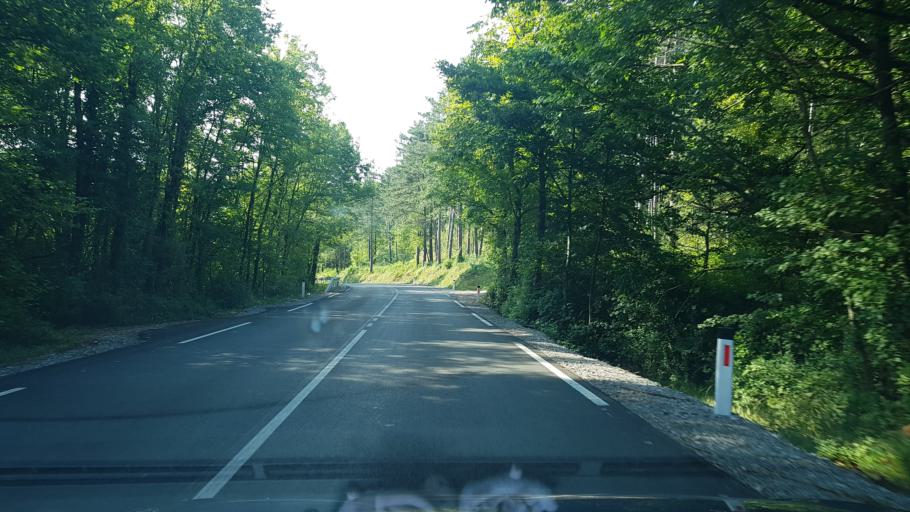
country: SI
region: Divaca
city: Divaca
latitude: 45.6673
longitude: 14.0181
